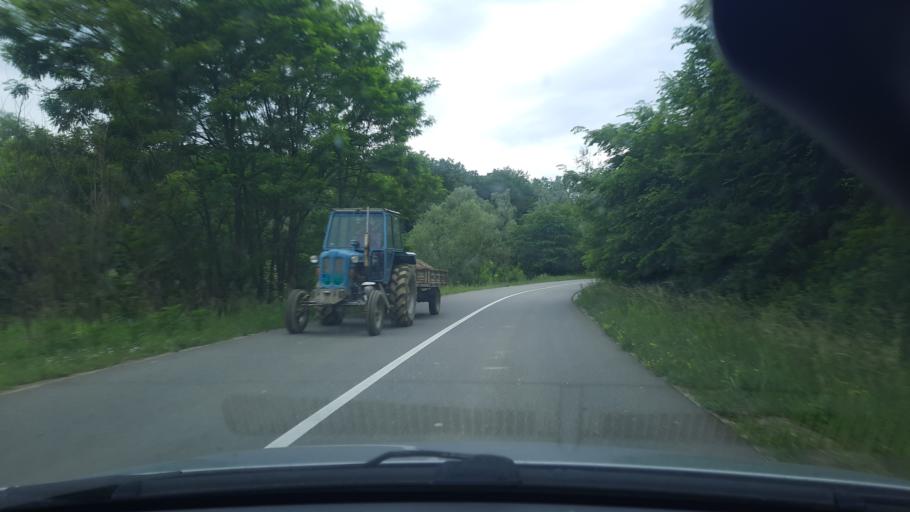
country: RS
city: Bukor
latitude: 44.5134
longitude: 19.5092
